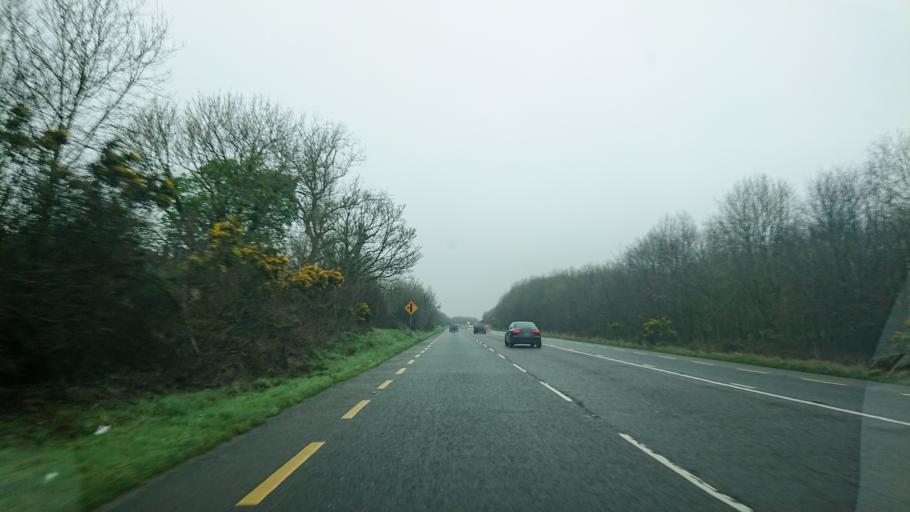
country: IE
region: Munster
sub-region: County Cork
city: Cork
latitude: 51.8189
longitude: -8.5339
